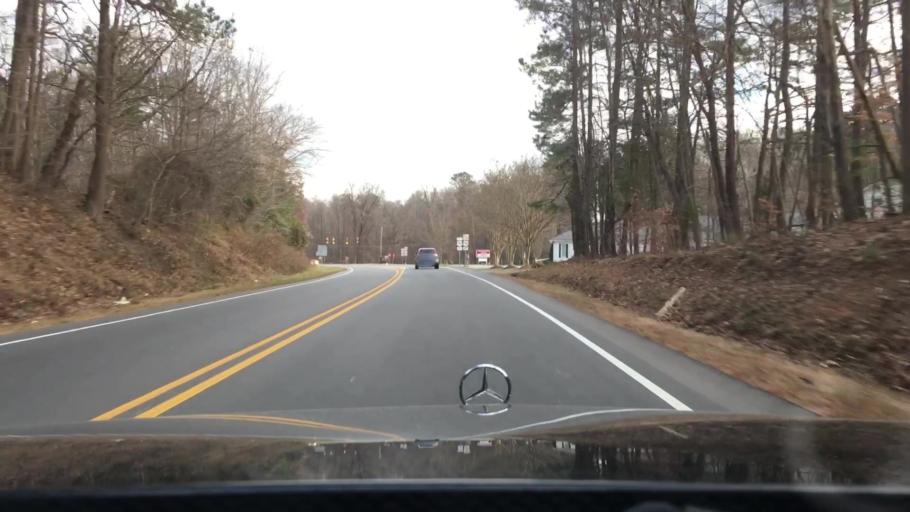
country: US
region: North Carolina
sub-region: Orange County
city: Hillsborough
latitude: 36.0576
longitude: -79.0513
